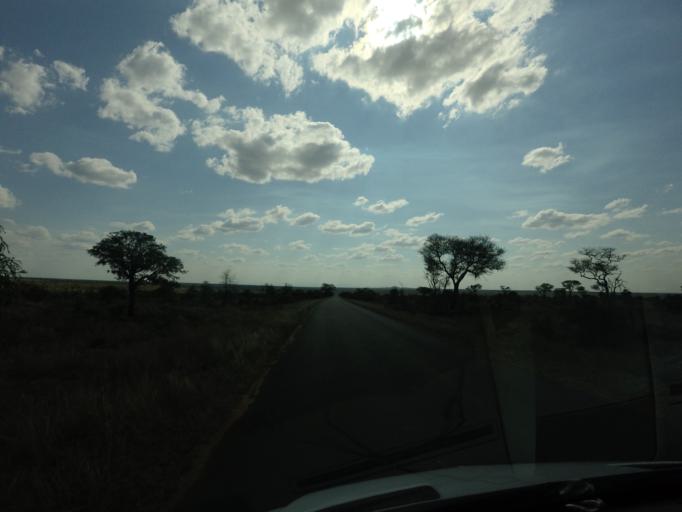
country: ZA
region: Limpopo
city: Thulamahashi
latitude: -24.3933
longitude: 31.6024
